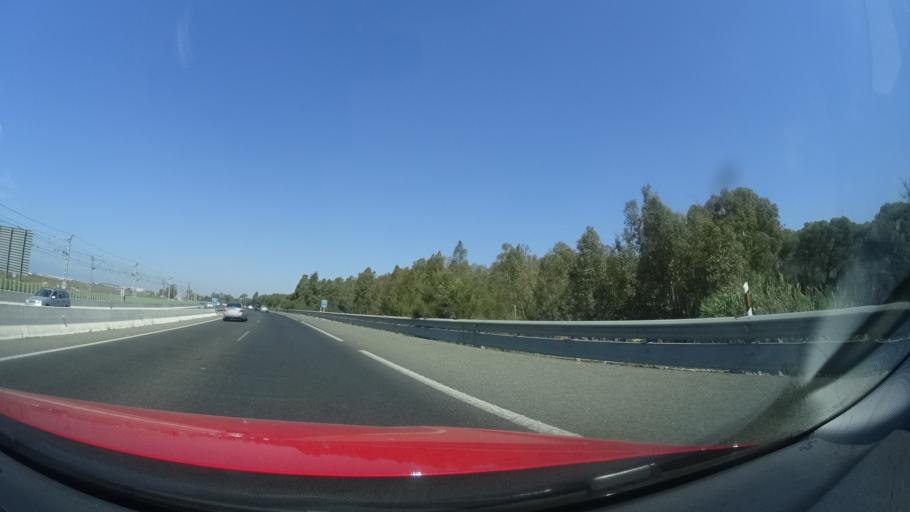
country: ES
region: Andalusia
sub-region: Provincia de Cadiz
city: Puerto Real
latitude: 36.5038
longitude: -6.1453
